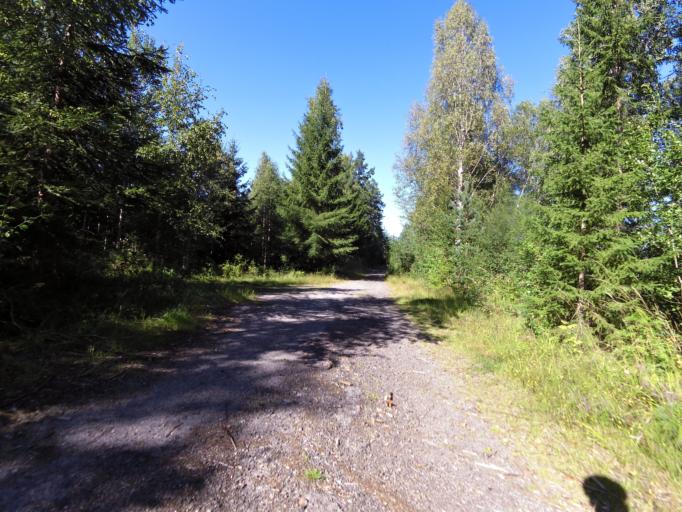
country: SE
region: Gaevleborg
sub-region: Sandvikens Kommun
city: Jarbo
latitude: 60.5634
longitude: 16.4866
